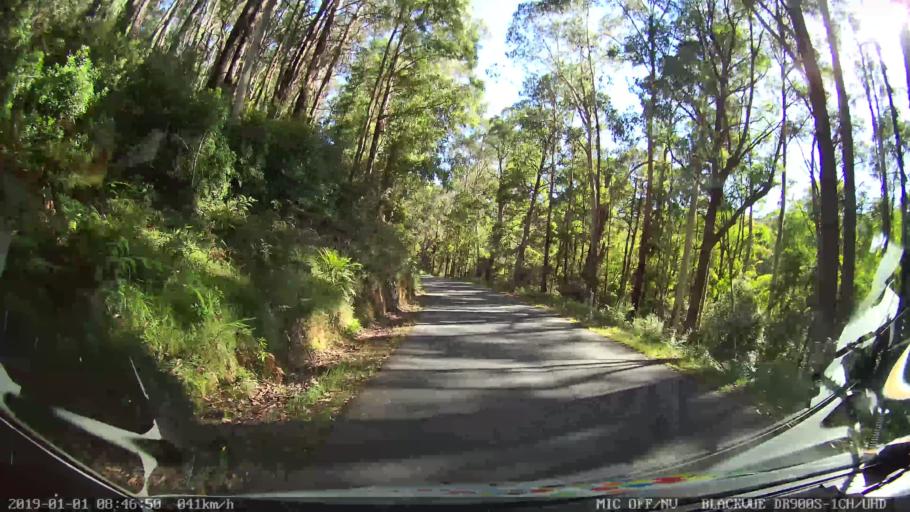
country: AU
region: New South Wales
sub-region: Snowy River
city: Jindabyne
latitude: -36.2978
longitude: 148.1948
